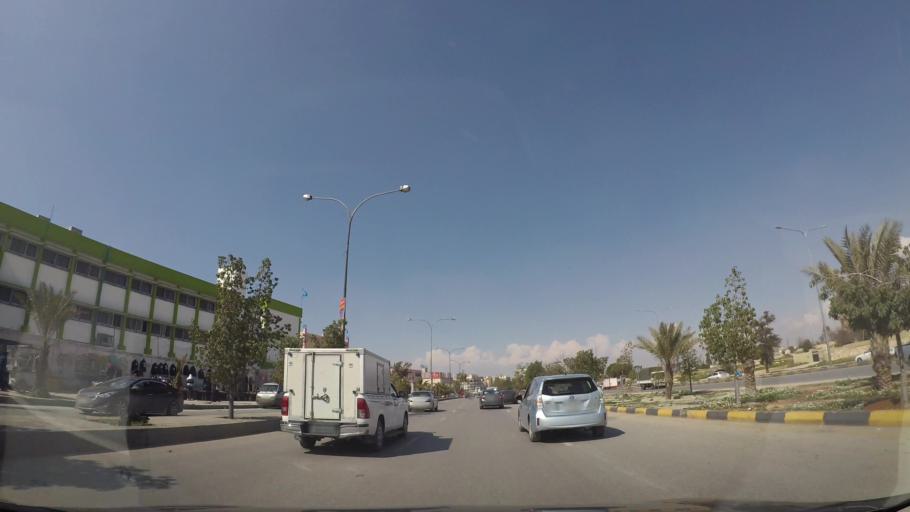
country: JO
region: Zarqa
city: Zarqa
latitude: 32.0573
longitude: 36.0947
